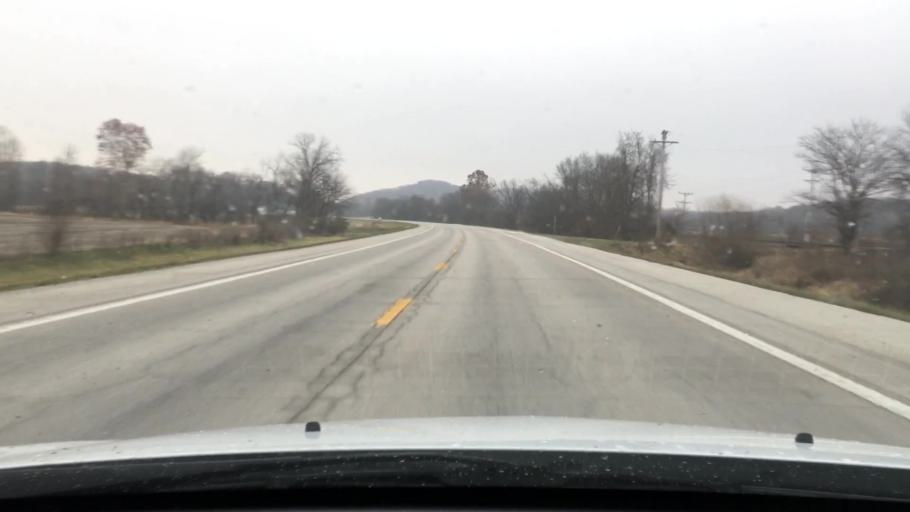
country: US
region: Missouri
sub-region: Pike County
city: Bowling Green
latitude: 39.3885
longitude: -91.1193
